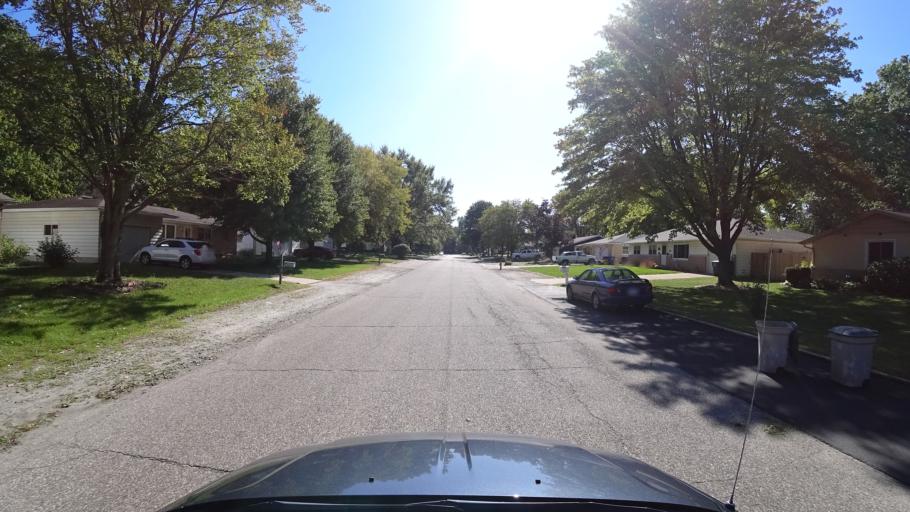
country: US
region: Indiana
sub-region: LaPorte County
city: Michigan City
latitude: 41.6935
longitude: -86.8829
